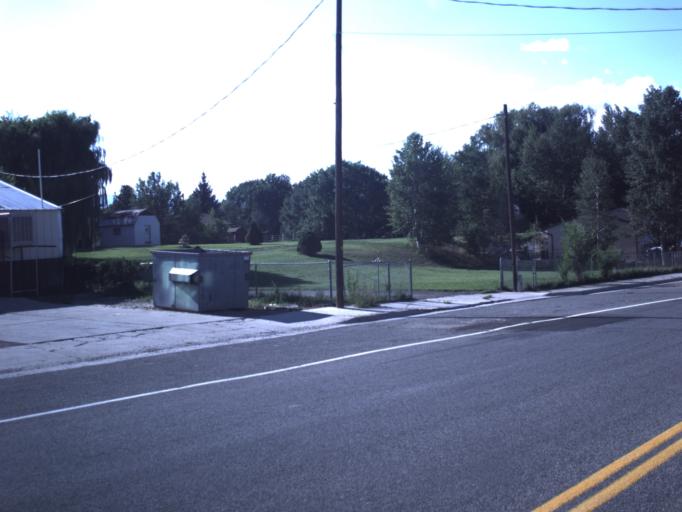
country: US
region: Utah
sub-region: Emery County
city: Huntington
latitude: 39.3491
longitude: -110.8519
